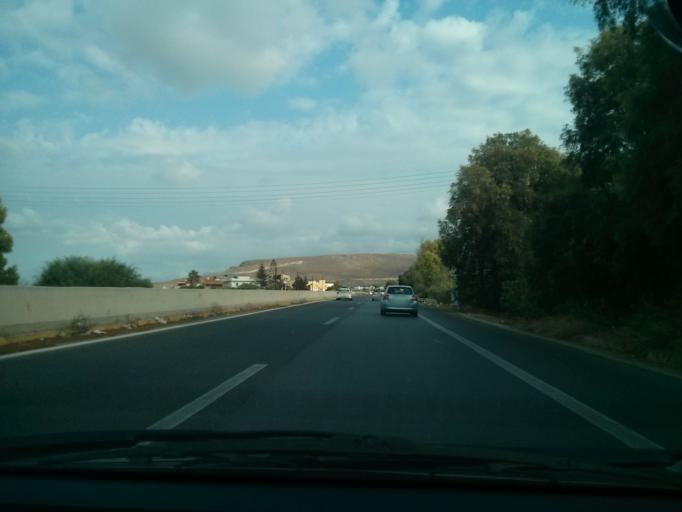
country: GR
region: Crete
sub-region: Nomos Irakleiou
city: Kokkini Hani
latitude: 35.3296
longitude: 25.2462
